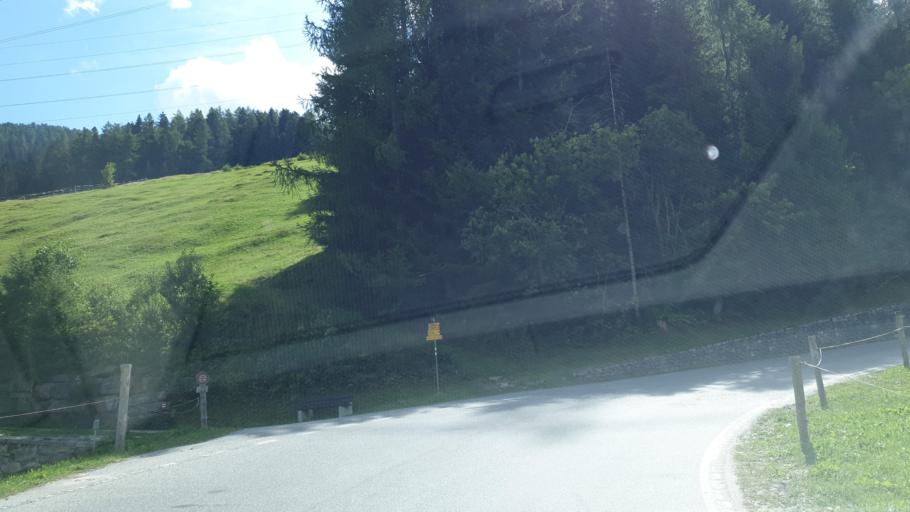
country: CH
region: Grisons
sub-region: Hinterrhein District
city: Hinterrhein
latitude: 46.5483
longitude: 9.3239
